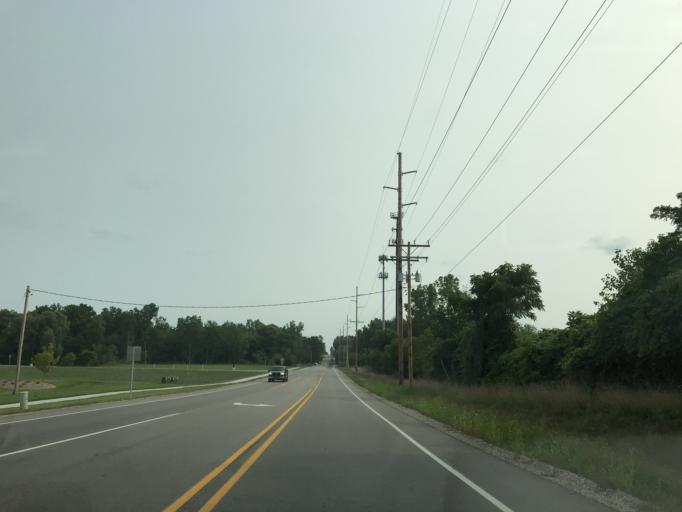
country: US
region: Michigan
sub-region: Ingham County
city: Okemos
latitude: 42.7506
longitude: -84.4477
